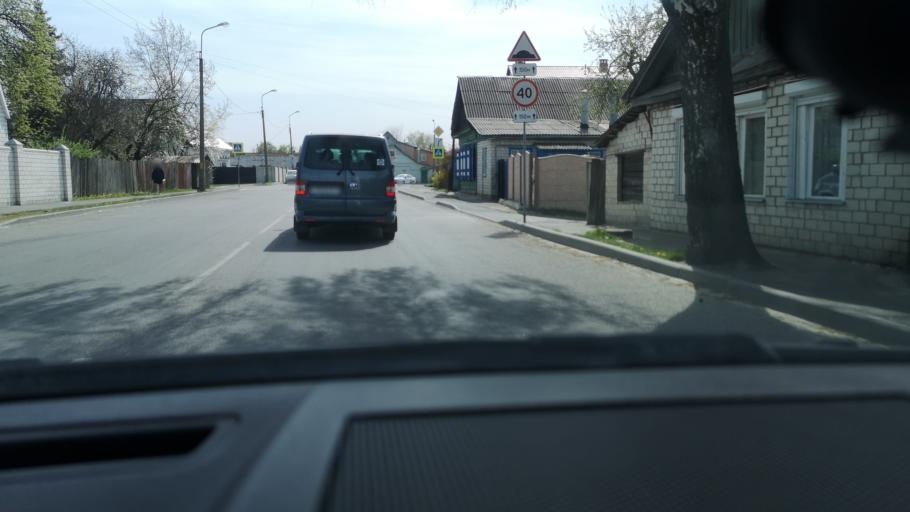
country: BY
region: Gomel
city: Gomel
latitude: 52.4150
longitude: 30.9848
